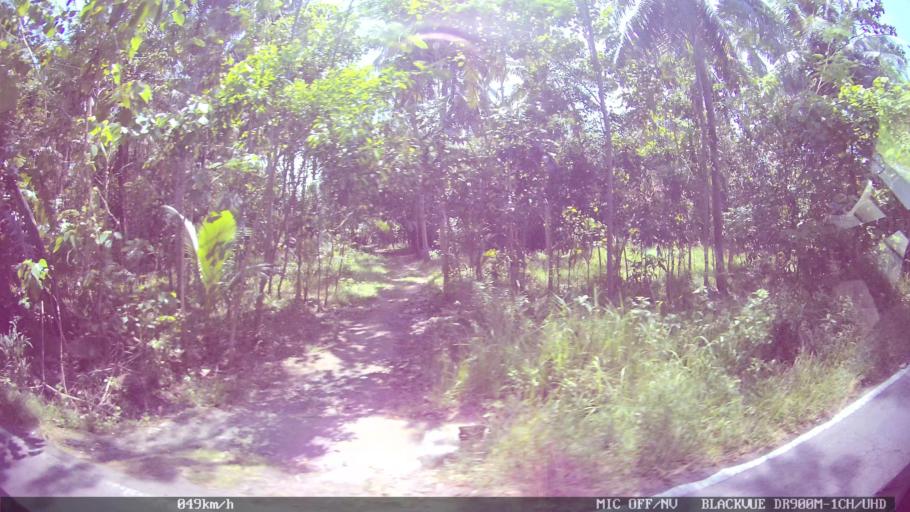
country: ID
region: Daerah Istimewa Yogyakarta
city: Srandakan
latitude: -7.8907
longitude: 110.0500
